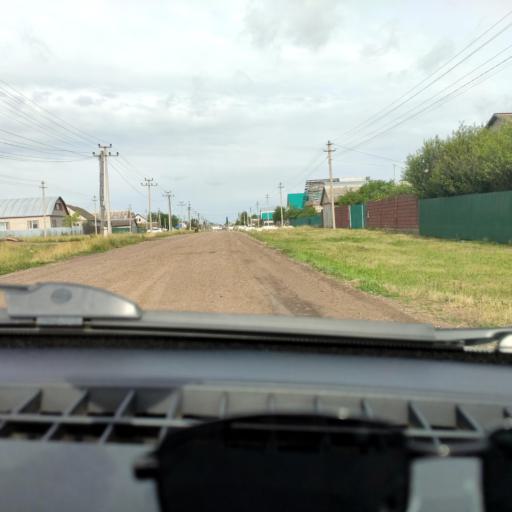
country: RU
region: Bashkortostan
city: Ulukulevo
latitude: 54.4209
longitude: 56.3374
